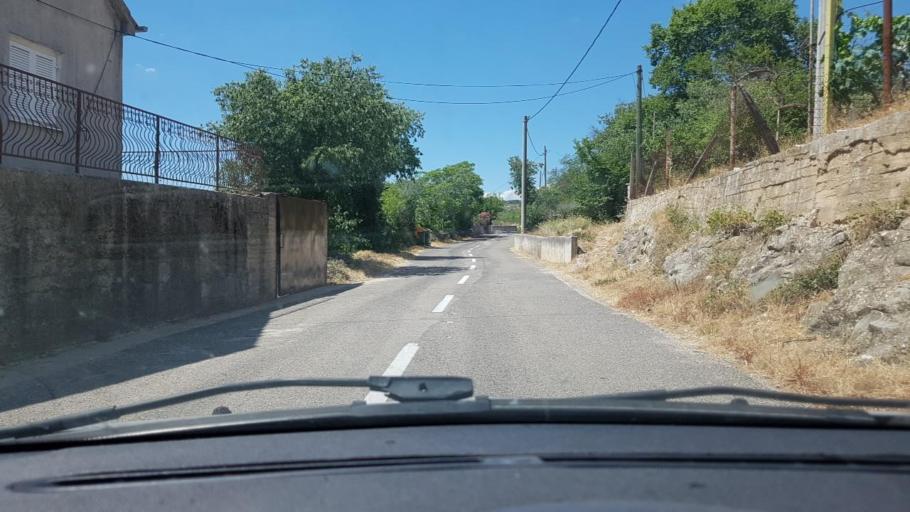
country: HR
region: Sibensko-Kniniska
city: Kistanje
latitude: 43.9089
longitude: 15.9195
